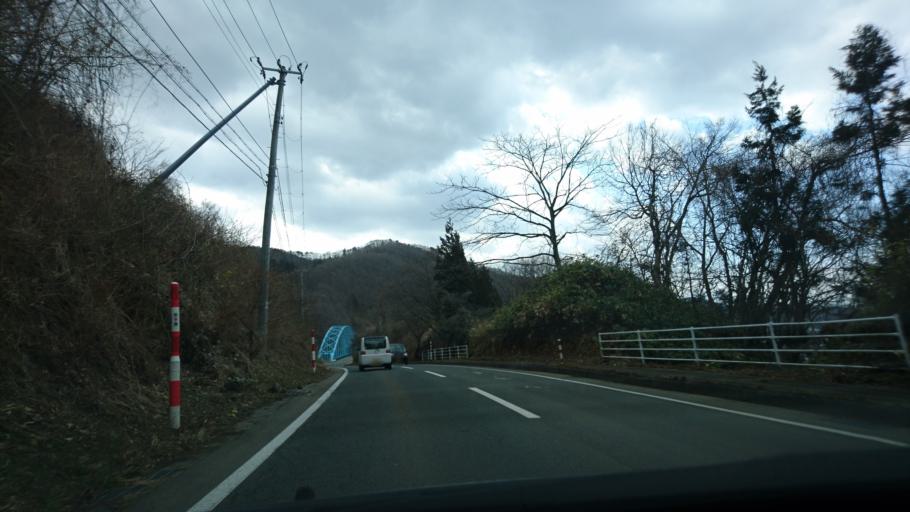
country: JP
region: Iwate
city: Shizukuishi
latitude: 39.6906
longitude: 141.0328
